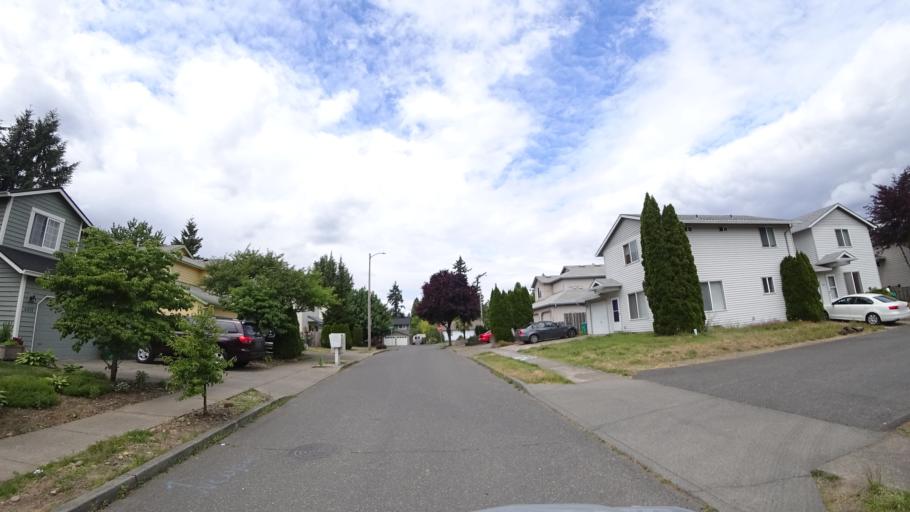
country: US
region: Oregon
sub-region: Clackamas County
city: Happy Valley
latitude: 45.4909
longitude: -122.5209
